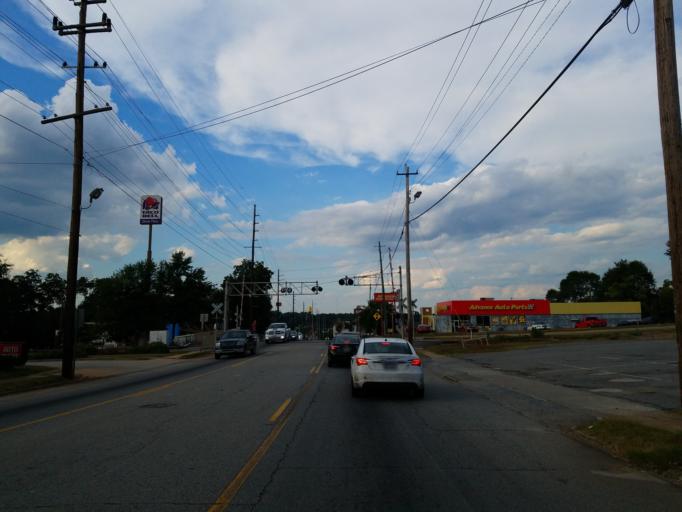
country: US
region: Georgia
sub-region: Monroe County
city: Forsyth
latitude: 33.0371
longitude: -83.9384
